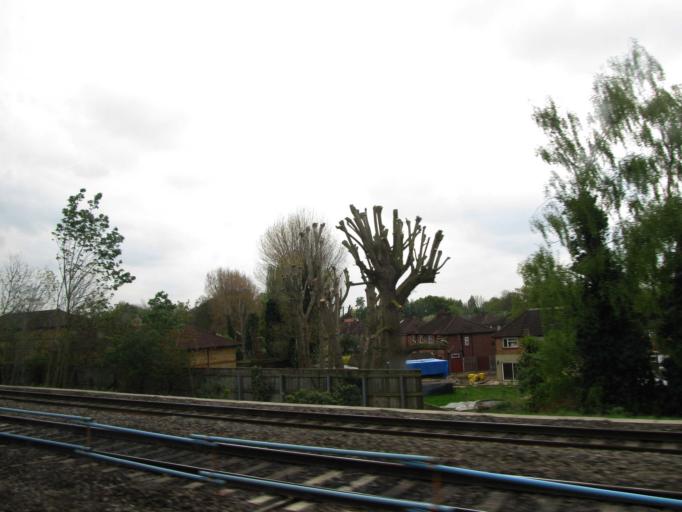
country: GB
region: England
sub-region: Greater London
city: West Drayton
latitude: 51.5101
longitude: -0.4796
